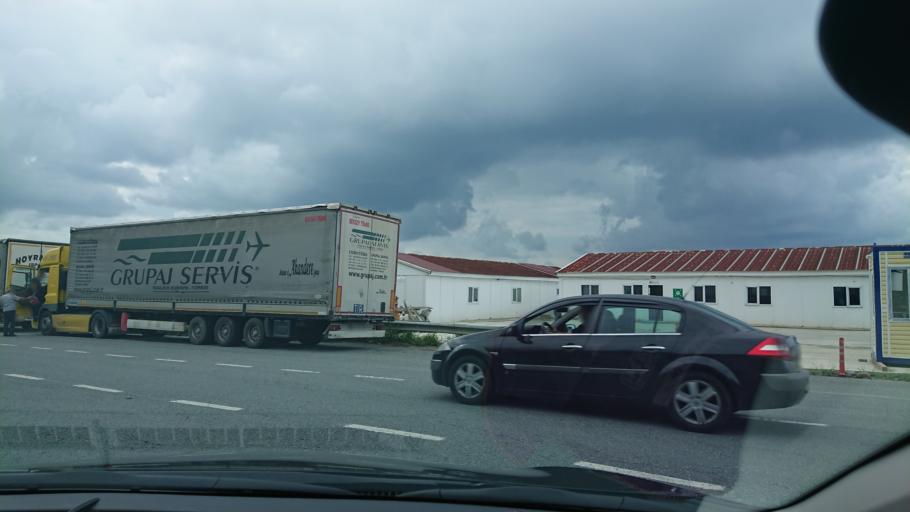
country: TR
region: Rize
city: Gundogdu
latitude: 41.0595
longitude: 40.6301
